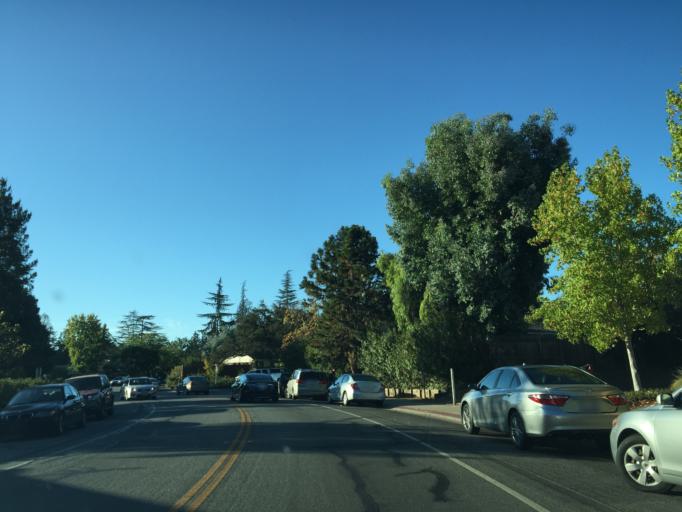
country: US
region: California
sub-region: Santa Clara County
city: Los Altos
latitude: 37.3939
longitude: -122.1214
